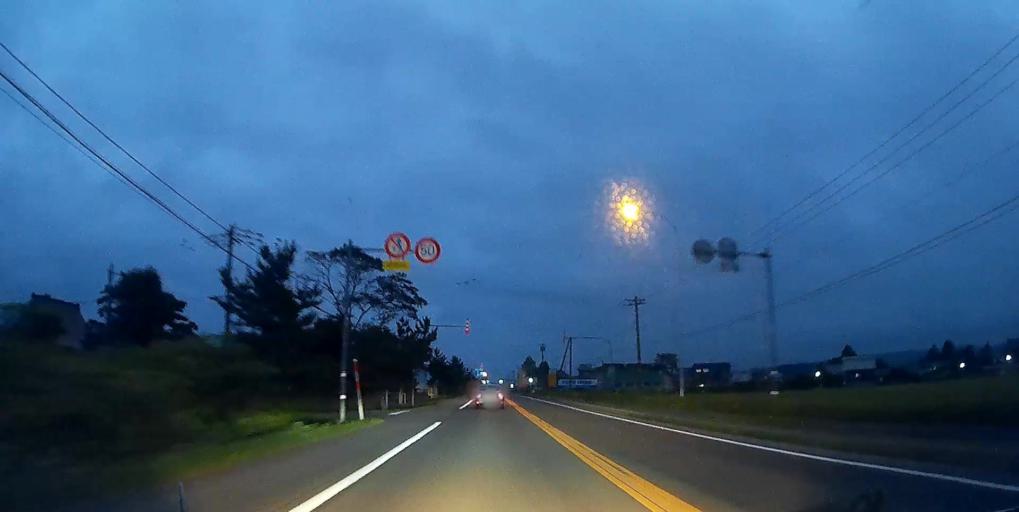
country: JP
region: Hokkaido
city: Nanae
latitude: 42.2198
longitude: 140.3767
